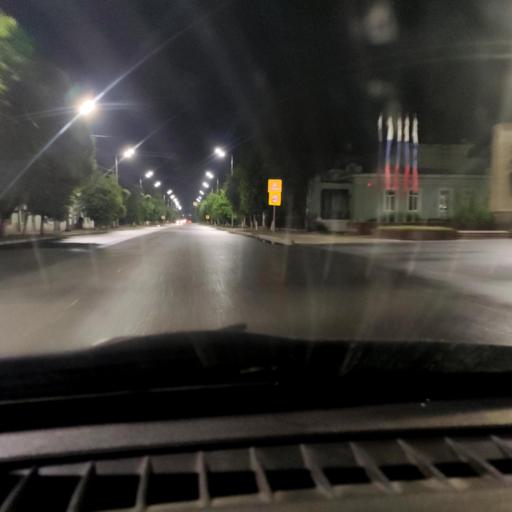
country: RU
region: Samara
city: Syzran'
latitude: 53.1561
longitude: 48.4754
